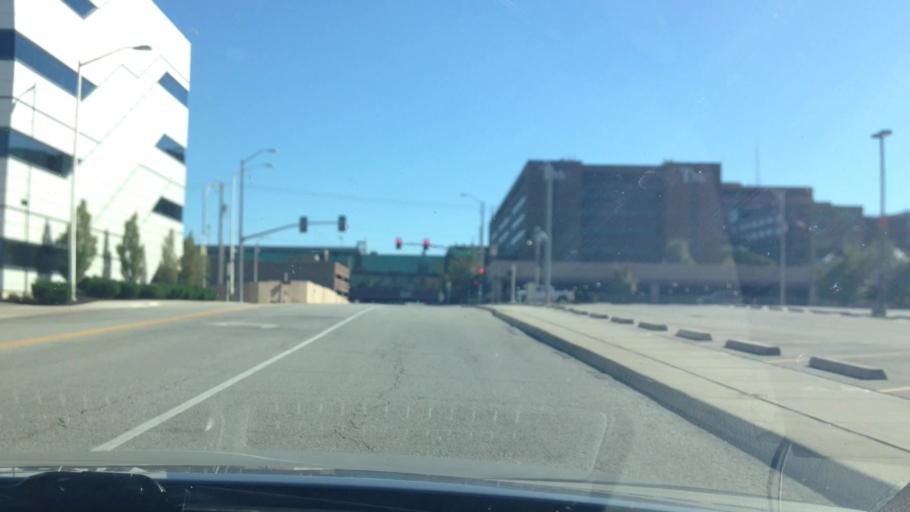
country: US
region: Missouri
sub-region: Jackson County
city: Kansas City
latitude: 39.0872
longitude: -94.5746
